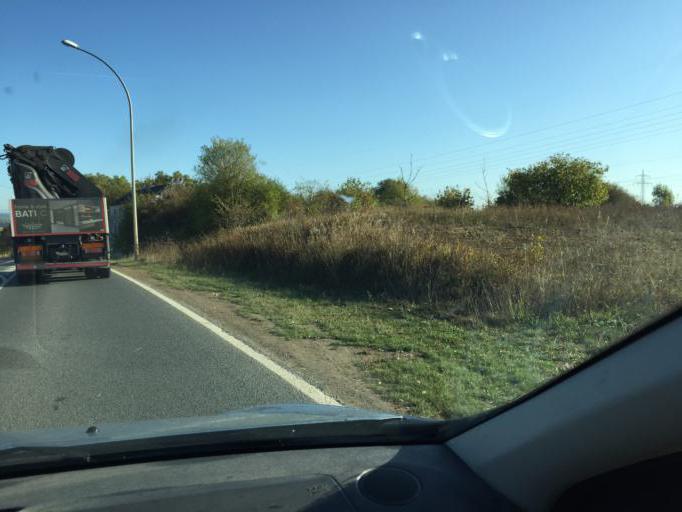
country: LU
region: Luxembourg
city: Colmar
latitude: 49.7890
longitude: 6.0969
